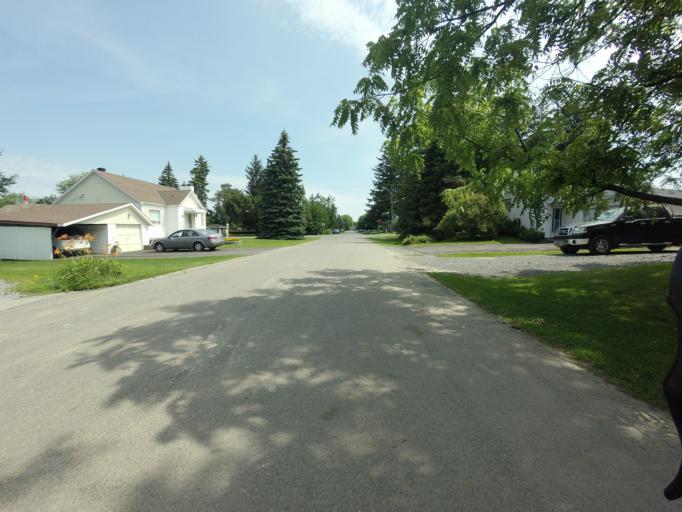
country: CA
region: Ontario
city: Ottawa
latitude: 45.3546
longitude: -75.7421
